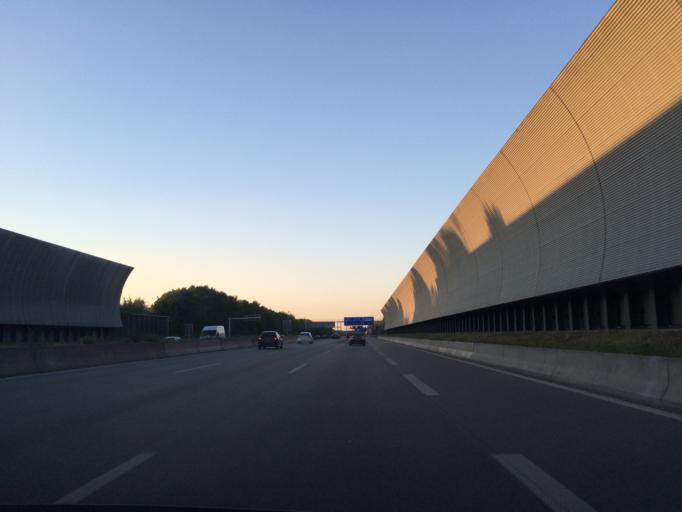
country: DE
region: Bavaria
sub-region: Upper Bavaria
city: Unterfoehring
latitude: 48.1987
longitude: 11.6182
